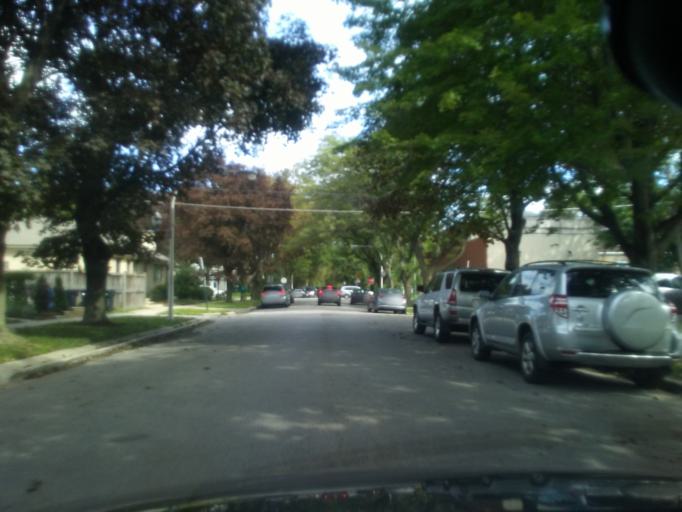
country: US
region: Illinois
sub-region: Cook County
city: Lincolnwood
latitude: 42.0042
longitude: -87.7022
